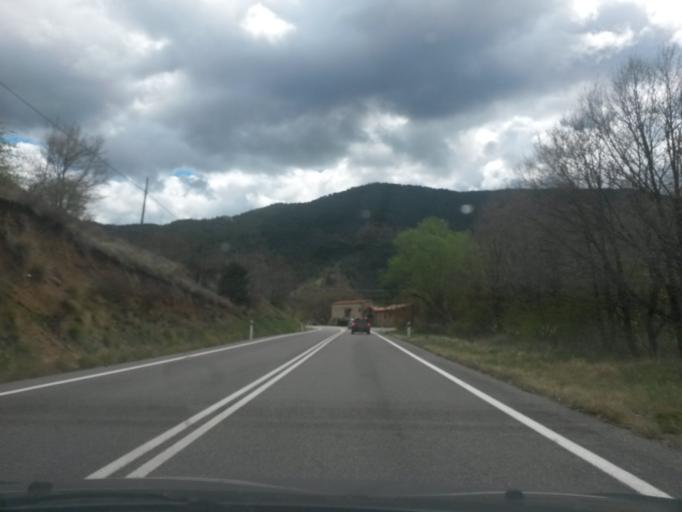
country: ES
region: Catalonia
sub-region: Provincia de Lleida
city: Toloriu
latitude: 42.3681
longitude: 1.6471
